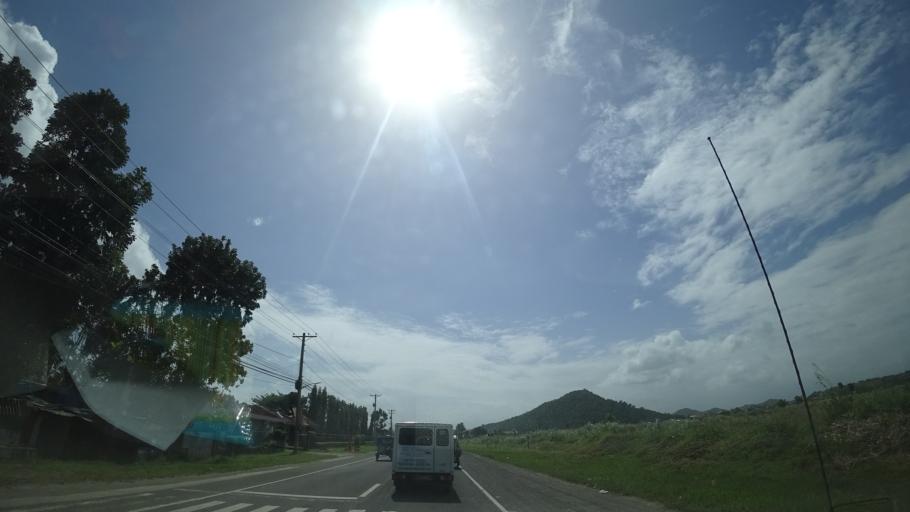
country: PH
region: Eastern Visayas
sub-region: Province of Leyte
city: Pawing
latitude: 11.1761
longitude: 125.0010
